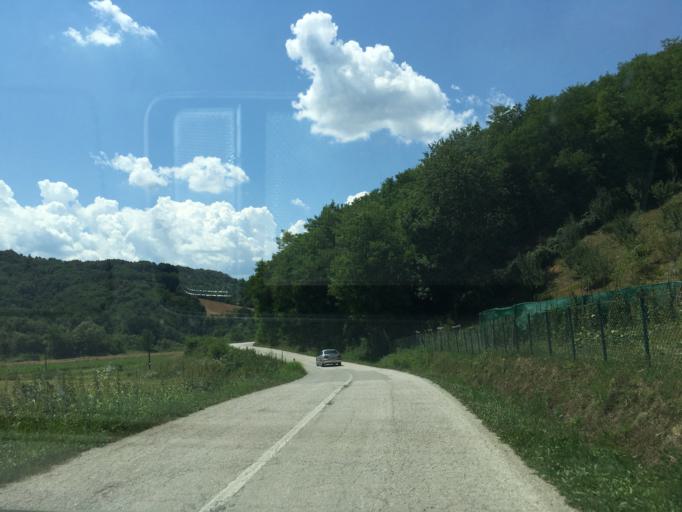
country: RS
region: Central Serbia
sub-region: Kolubarski Okrug
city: Ljig
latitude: 44.2410
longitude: 20.3744
